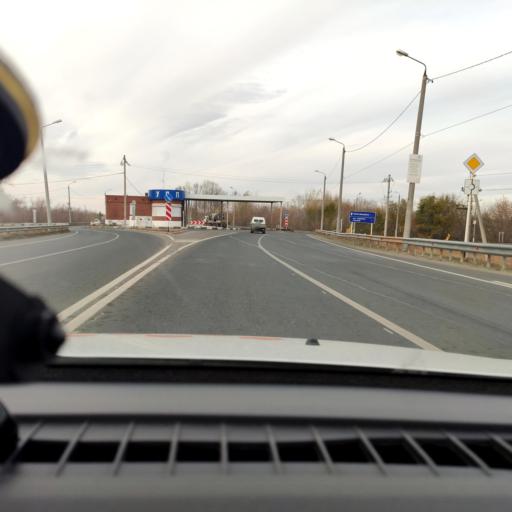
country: RU
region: Samara
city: Novokuybyshevsk
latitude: 53.1430
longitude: 49.9876
